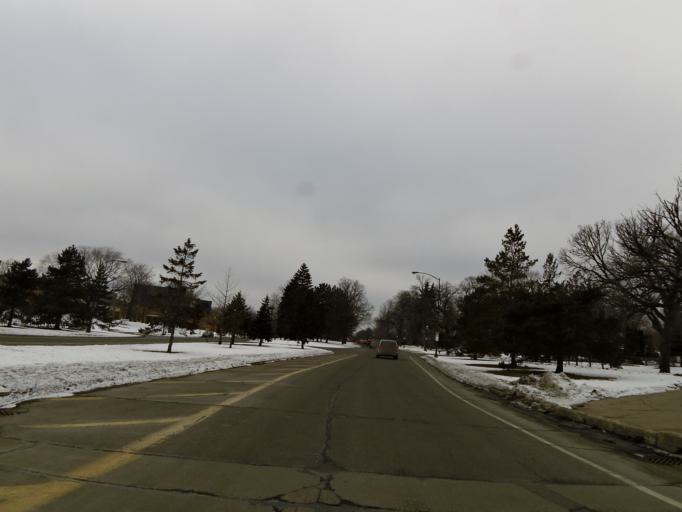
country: US
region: Minnesota
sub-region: Ramsey County
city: Falcon Heights
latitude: 44.9415
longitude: -93.1532
